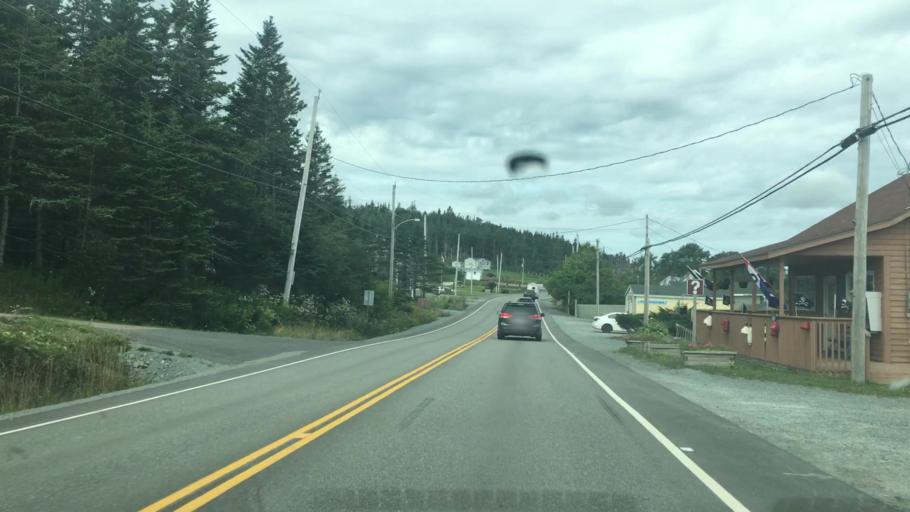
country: CA
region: Nova Scotia
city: Princeville
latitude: 45.6529
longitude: -60.8596
